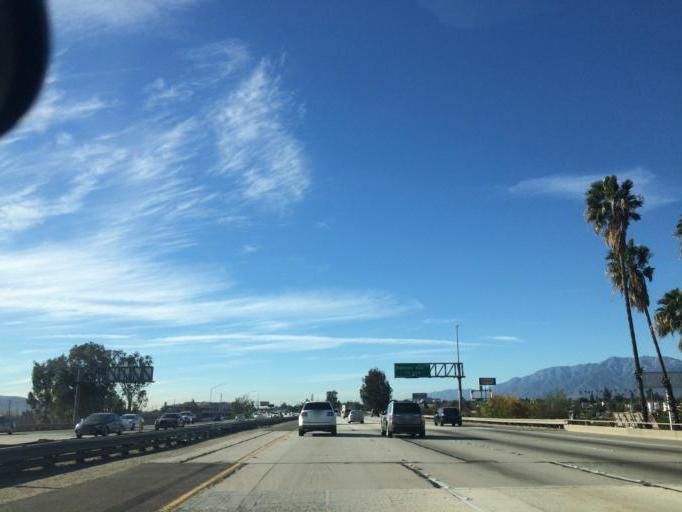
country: US
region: California
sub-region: San Bernardino County
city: Colton
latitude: 34.0658
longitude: -117.3225
